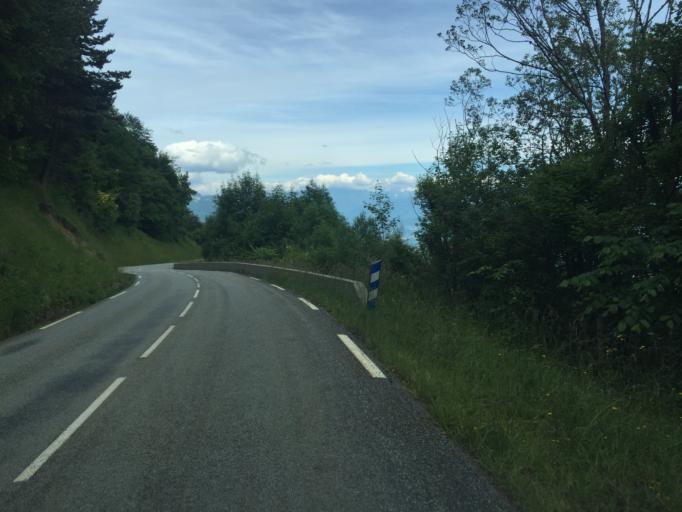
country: FR
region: Rhone-Alpes
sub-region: Departement de la Savoie
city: Saint-Baldoph
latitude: 45.4879
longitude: 5.9194
